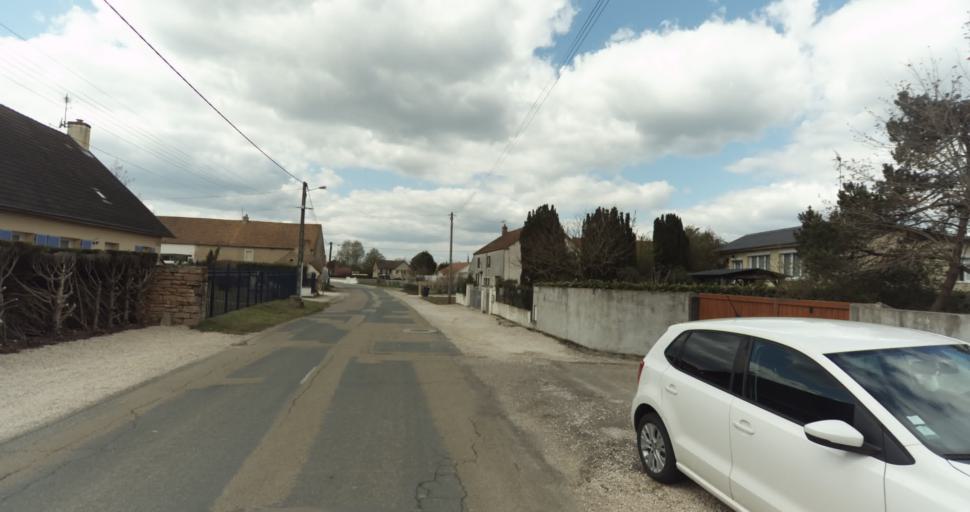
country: FR
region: Bourgogne
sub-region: Departement de la Cote-d'Or
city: Auxonne
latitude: 47.1889
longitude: 5.4017
